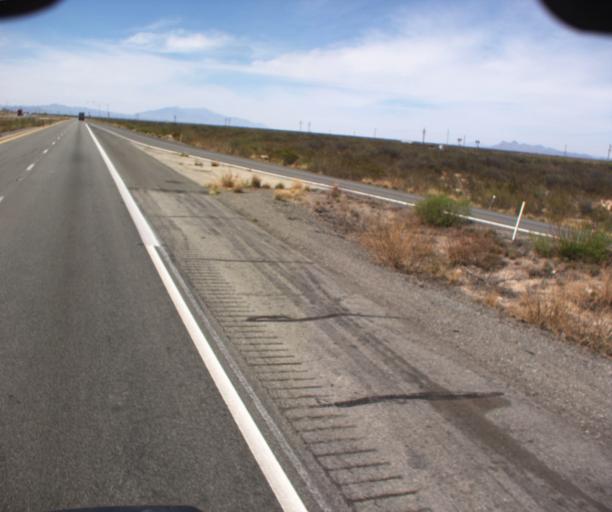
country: US
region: New Mexico
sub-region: Hidalgo County
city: Lordsburg
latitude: 32.2724
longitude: -109.2505
